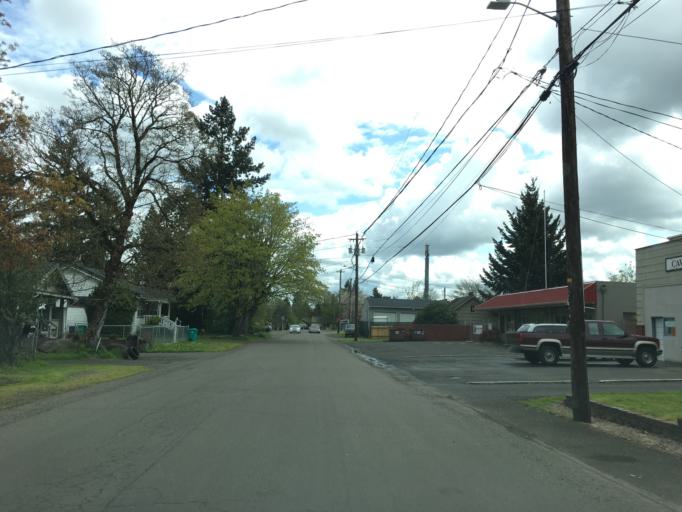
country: US
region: Oregon
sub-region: Multnomah County
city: Portland
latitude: 45.5566
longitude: -122.6025
